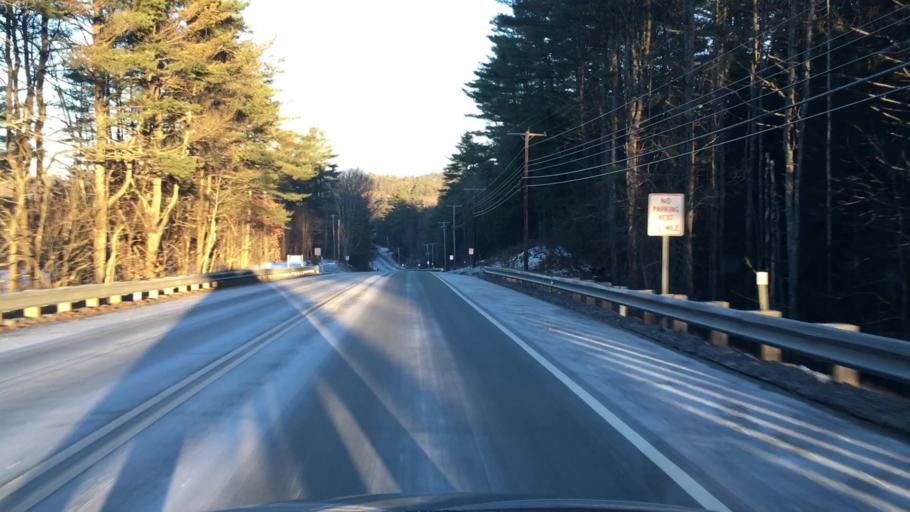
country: US
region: New Hampshire
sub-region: Grafton County
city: Hanover
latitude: 43.7307
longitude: -72.2637
